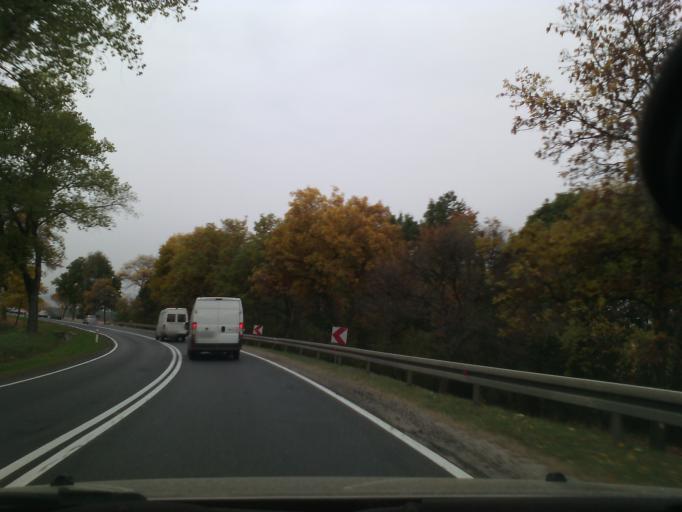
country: PL
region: Lower Silesian Voivodeship
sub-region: Powiat walbrzyski
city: Stare Bogaczowice
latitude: 50.9140
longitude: 16.1953
